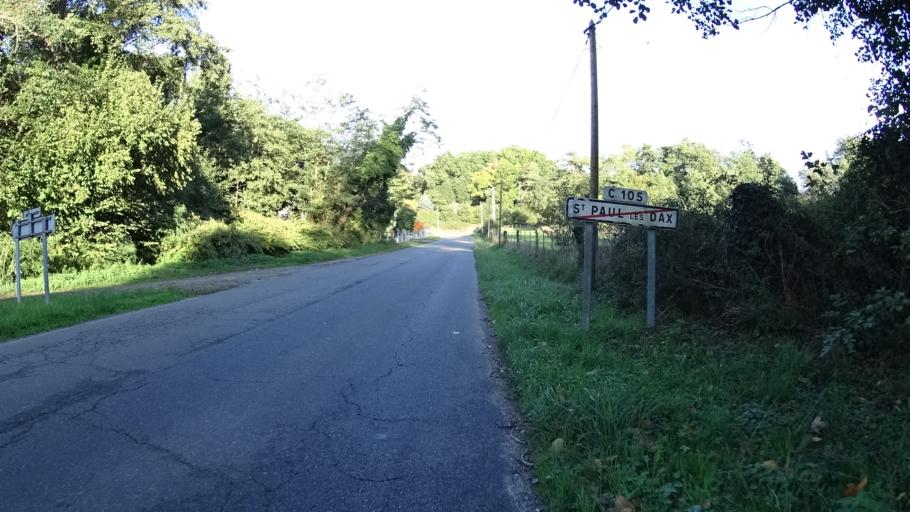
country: FR
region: Aquitaine
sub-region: Departement des Landes
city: Saint-Paul-les-Dax
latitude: 43.7386
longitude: -1.0426
